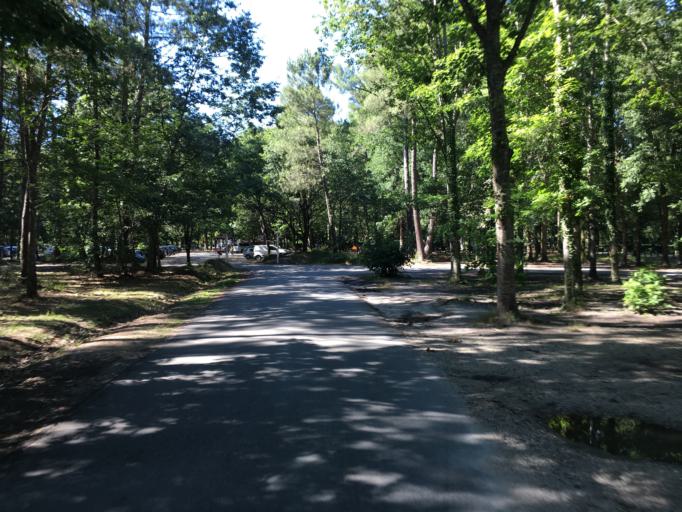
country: FR
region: Aquitaine
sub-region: Departement de la Gironde
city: Belin-Beliet
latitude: 44.4958
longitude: -0.6489
